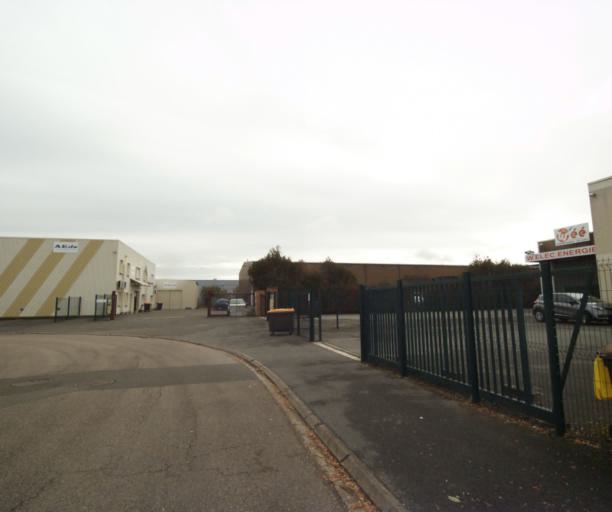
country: FR
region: Centre
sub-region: Departement d'Eure-et-Loir
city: Dreux
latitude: 48.7475
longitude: 1.3539
